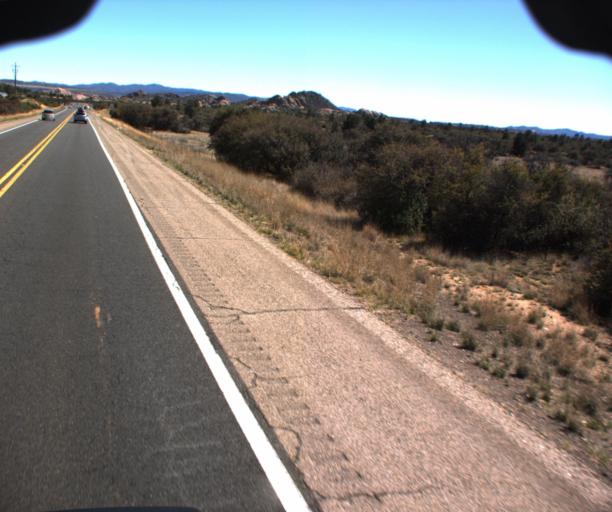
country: US
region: Arizona
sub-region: Yavapai County
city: Prescott
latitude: 34.6396
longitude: -112.4312
